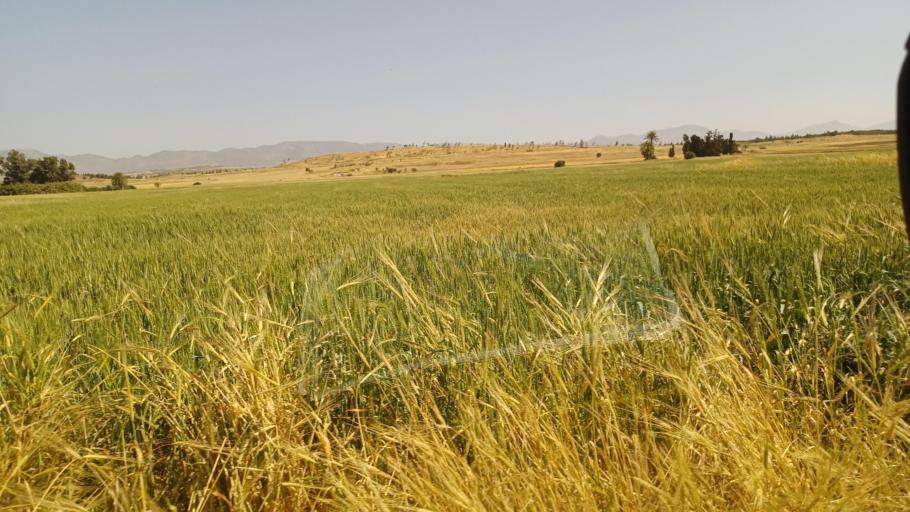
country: CY
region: Lefkosia
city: Mammari
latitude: 35.1803
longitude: 33.2144
